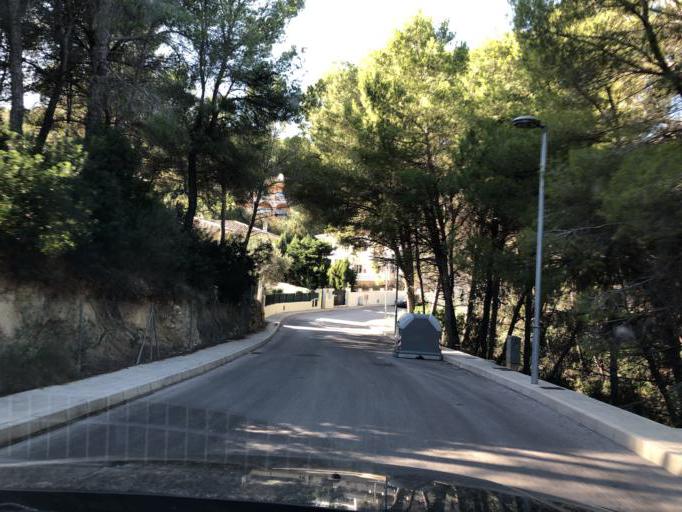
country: ES
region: Balearic Islands
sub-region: Illes Balears
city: Camp de Mar
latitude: 39.5405
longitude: 2.4089
